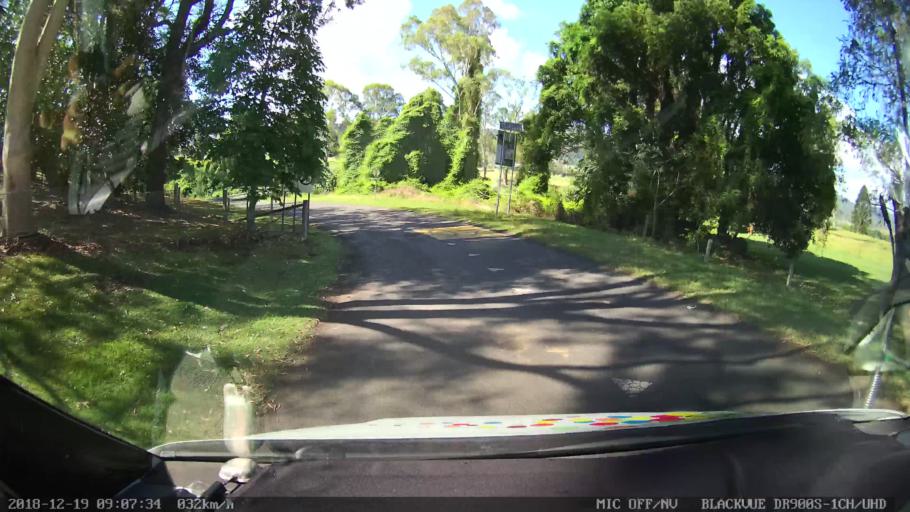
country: AU
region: New South Wales
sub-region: Kyogle
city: Kyogle
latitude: -28.4762
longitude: 152.9332
